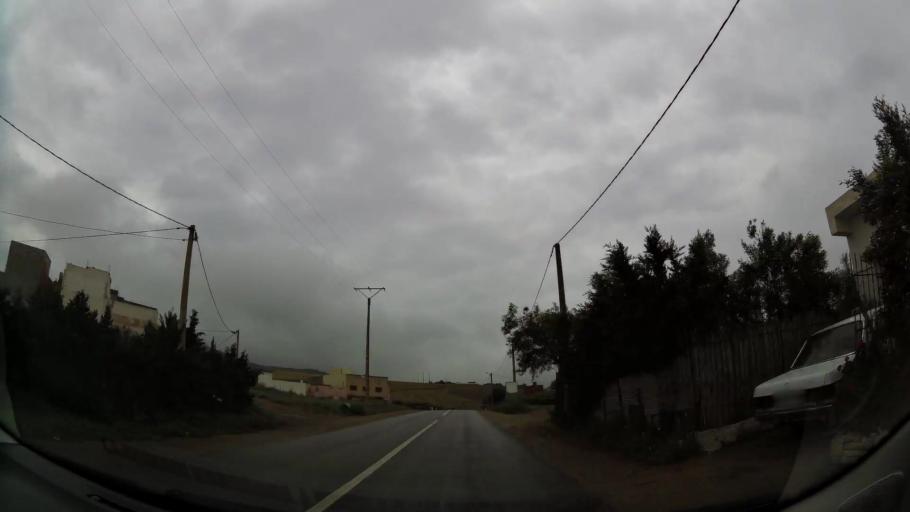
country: MA
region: Oriental
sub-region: Nador
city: Nador
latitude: 35.1411
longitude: -3.0464
